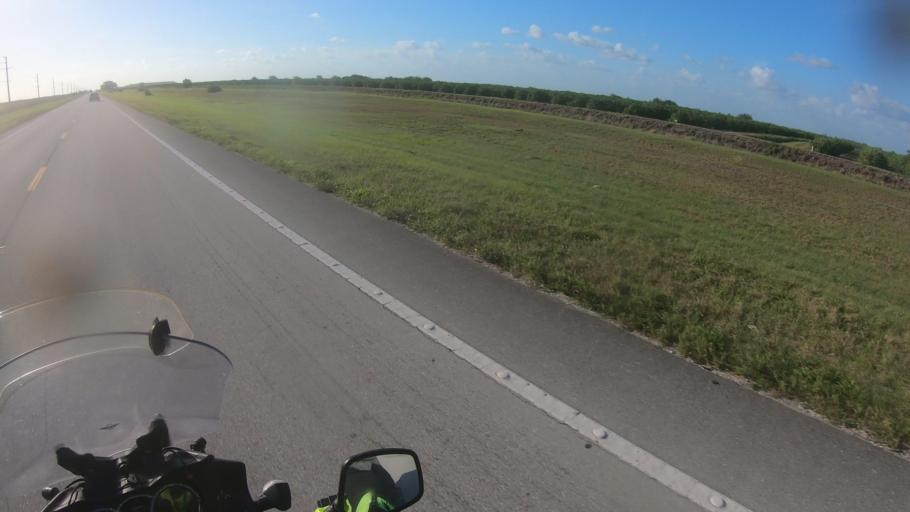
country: US
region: Florida
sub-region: Highlands County
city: Placid Lakes
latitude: 27.2097
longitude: -81.5844
